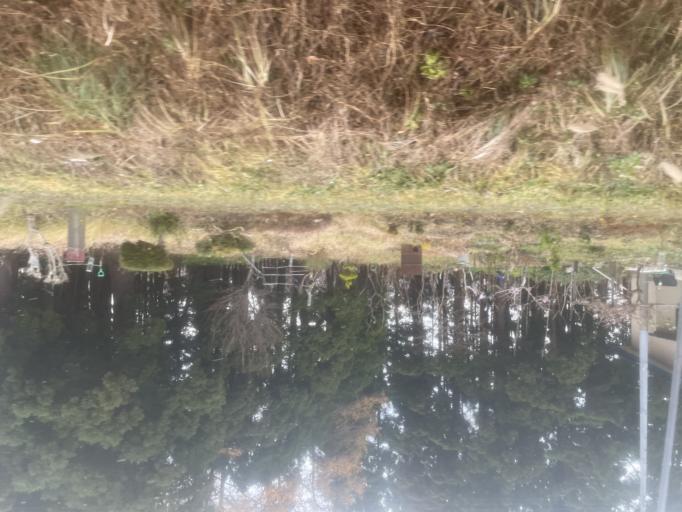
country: JP
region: Aomori
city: Goshogawara
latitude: 41.1804
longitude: 140.4761
